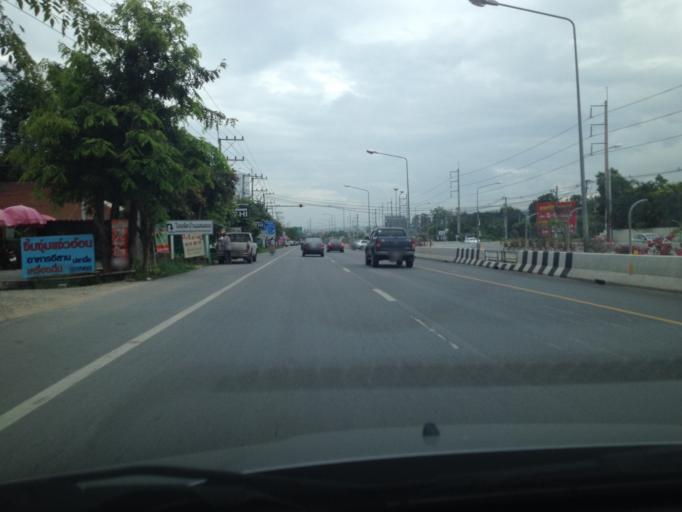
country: TH
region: Chiang Mai
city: Hang Dong
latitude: 18.7408
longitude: 98.9362
